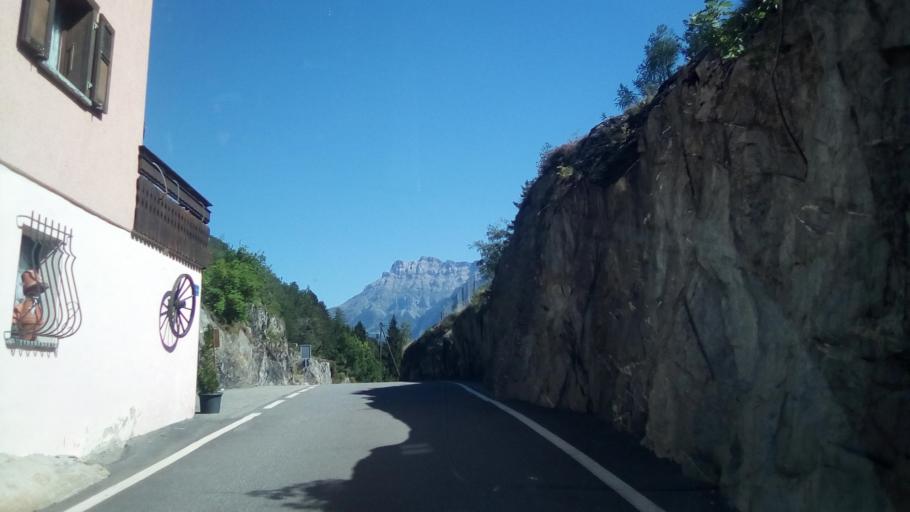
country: CH
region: Valais
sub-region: Saint-Maurice District
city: Salvan
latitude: 46.1086
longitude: 7.0083
